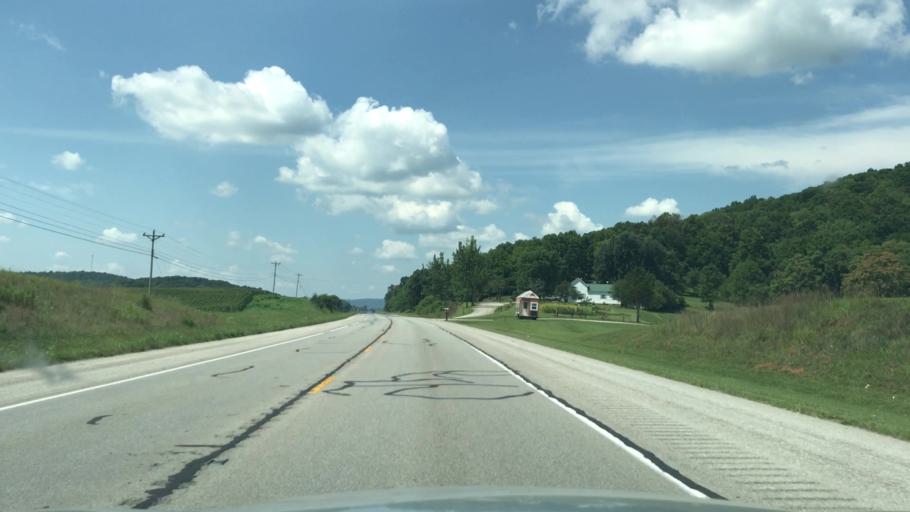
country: US
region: Kentucky
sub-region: Wayne County
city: Monticello
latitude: 36.8006
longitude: -84.9239
